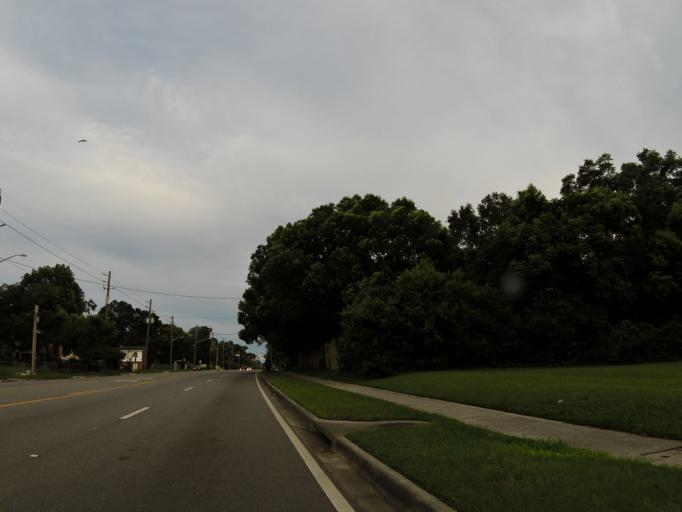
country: US
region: Florida
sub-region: Duval County
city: Jacksonville
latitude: 30.3883
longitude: -81.7176
